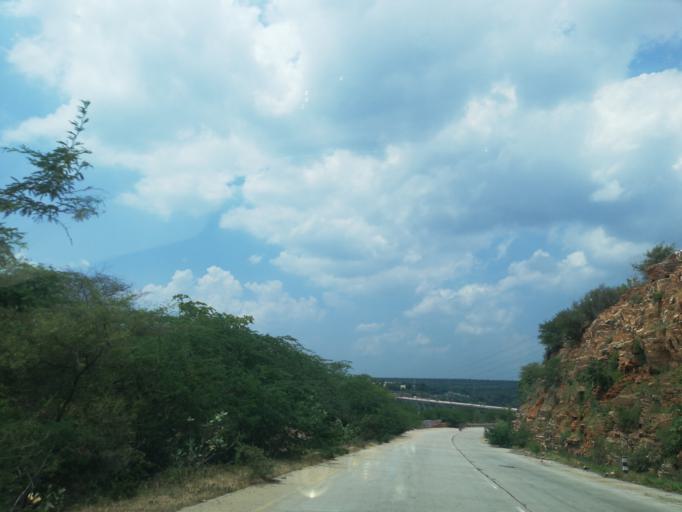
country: IN
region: Andhra Pradesh
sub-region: Guntur
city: Macherla
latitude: 16.5729
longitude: 79.3309
